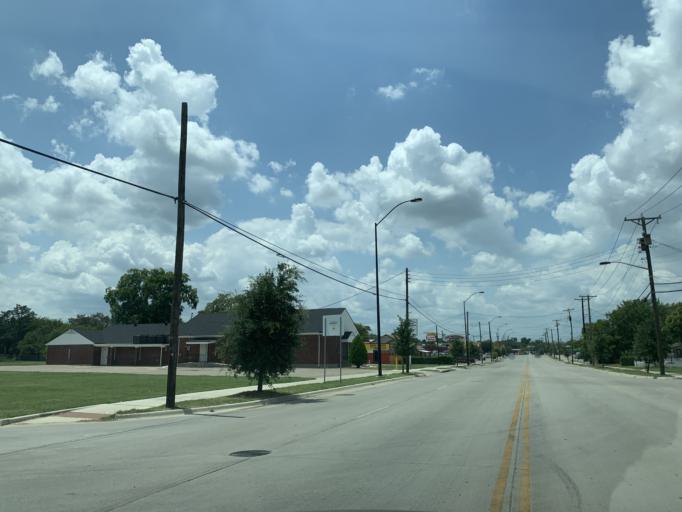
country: US
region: Texas
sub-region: Tarrant County
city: Fort Worth
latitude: 32.7313
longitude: -97.2663
